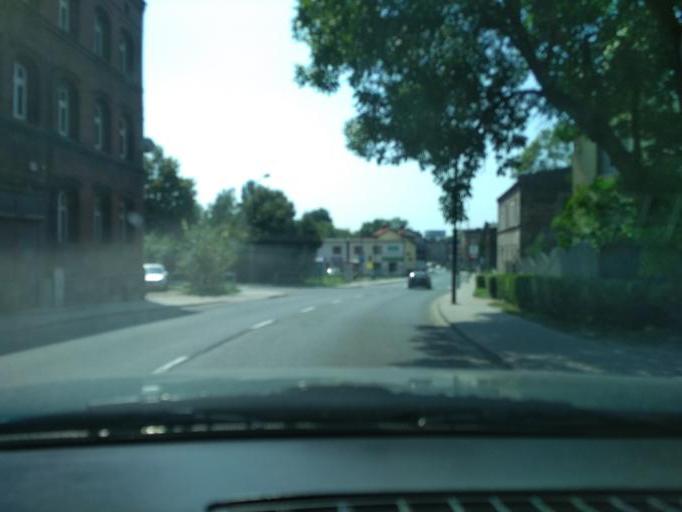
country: PL
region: Silesian Voivodeship
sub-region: Katowice
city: Katowice
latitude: 50.2801
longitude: 19.0060
